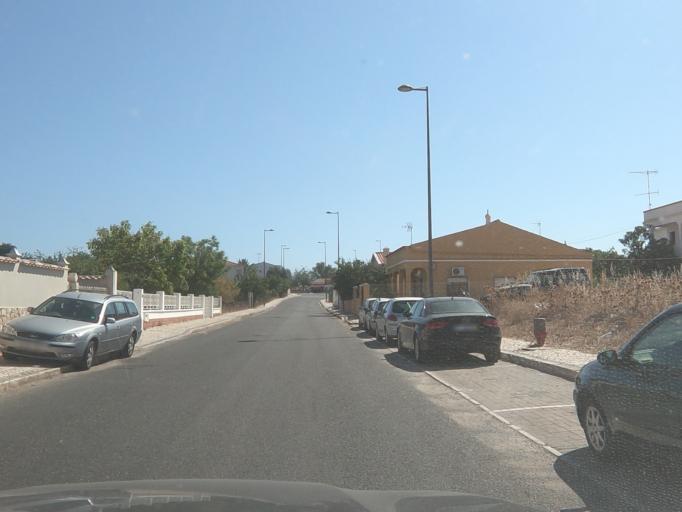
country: PT
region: Faro
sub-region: Faro
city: Santa Barbara de Nexe
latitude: 37.0877
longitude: -7.9889
